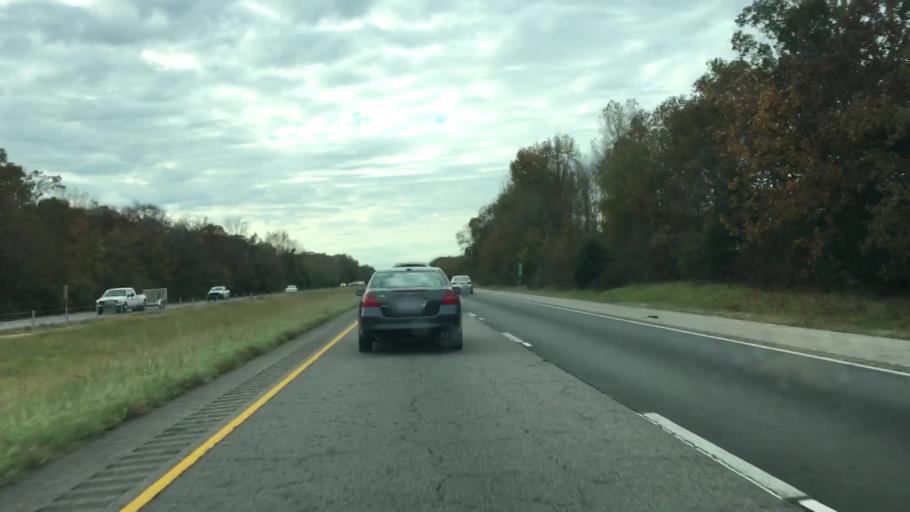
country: US
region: Arkansas
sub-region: Conway County
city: Morrilton
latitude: 35.1608
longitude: -92.5963
